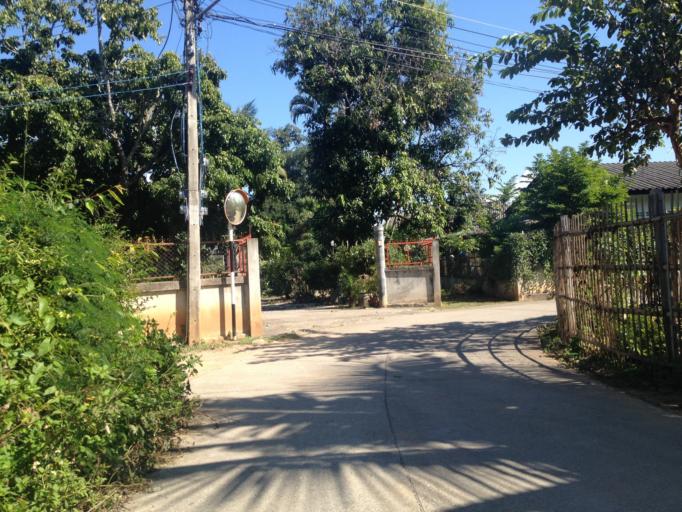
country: TH
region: Chiang Mai
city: Hang Dong
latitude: 18.6961
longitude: 98.9311
